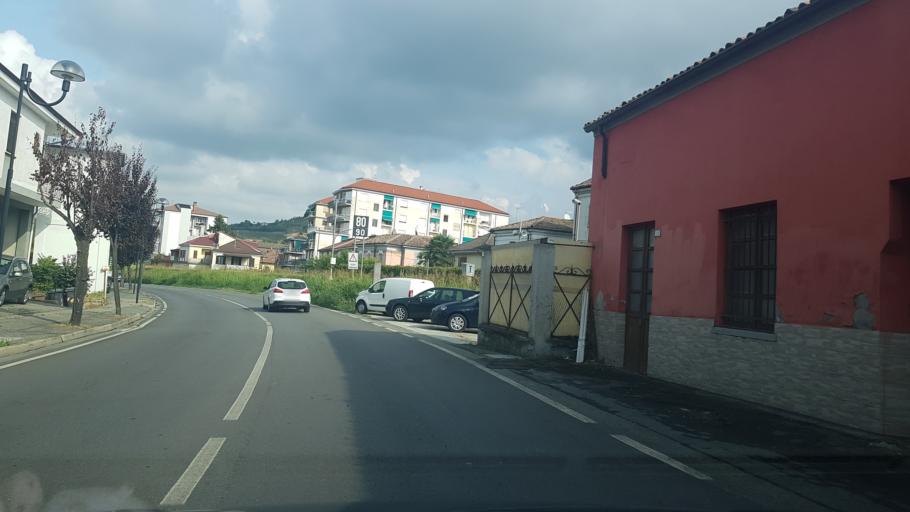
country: IT
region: Piedmont
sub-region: Provincia di Asti
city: Canelli
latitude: 44.7153
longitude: 8.2902
